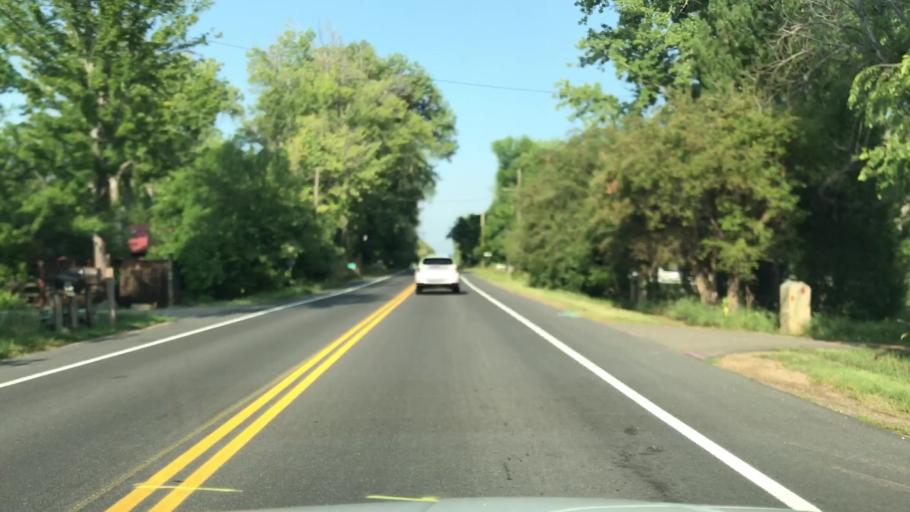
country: US
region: Colorado
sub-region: Boulder County
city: Gunbarrel
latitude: 40.0345
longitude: -105.1713
